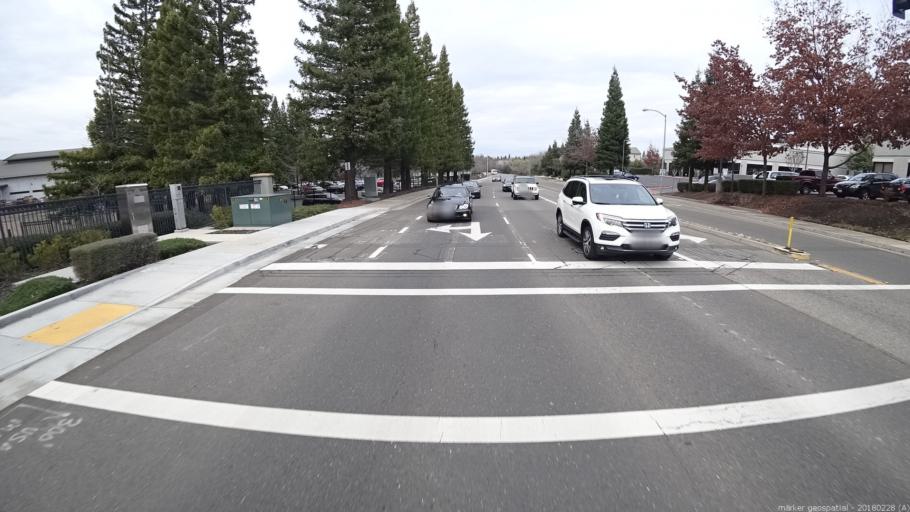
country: US
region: California
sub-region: Sacramento County
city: Folsom
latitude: 38.6594
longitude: -121.1698
